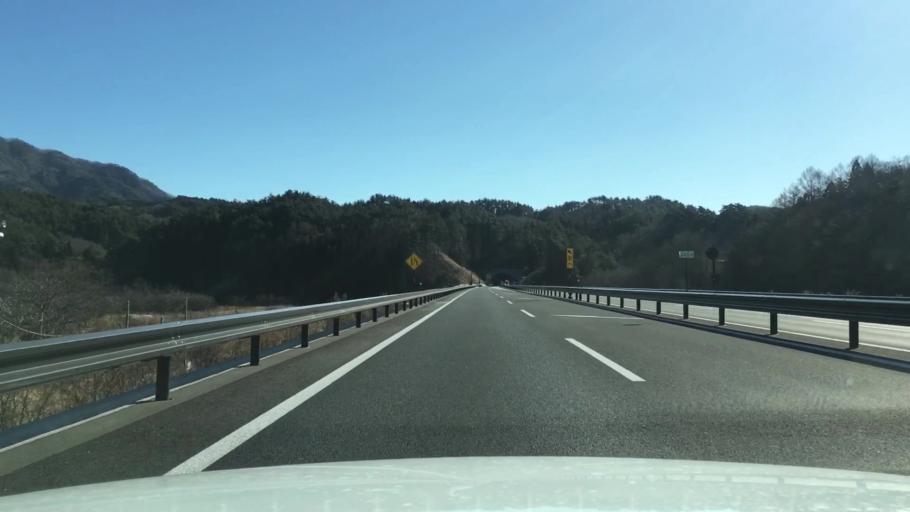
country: JP
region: Iwate
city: Yamada
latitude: 39.5173
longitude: 141.9393
